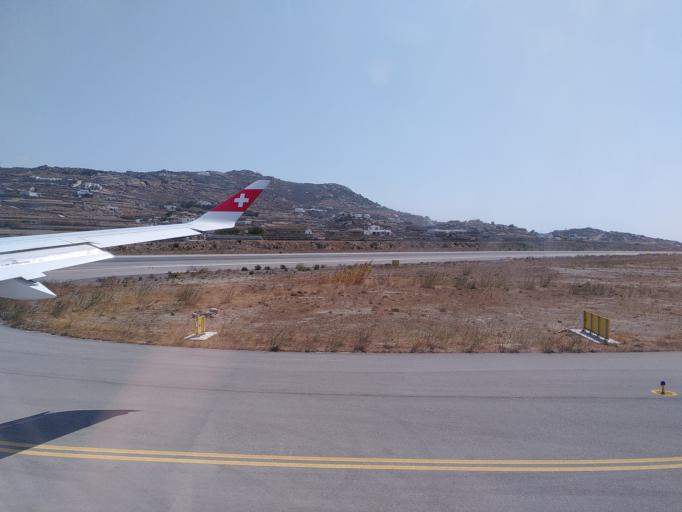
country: GR
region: South Aegean
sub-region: Nomos Kykladon
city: Mykonos
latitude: 37.4363
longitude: 25.3470
